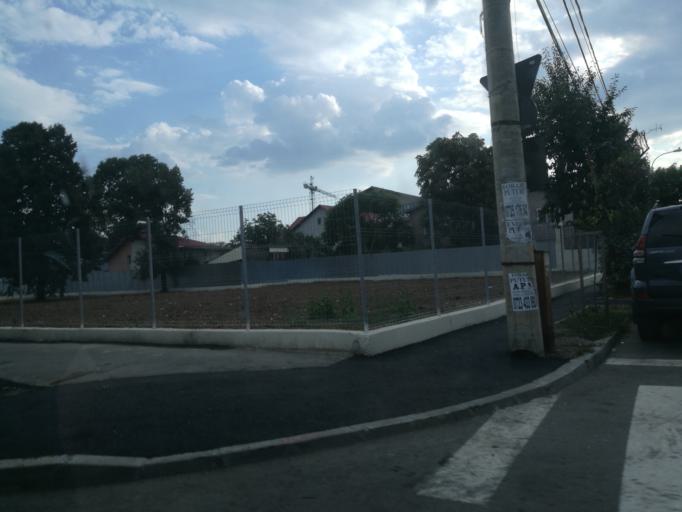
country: RO
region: Ilfov
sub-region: Comuna Chiajna
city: Rosu
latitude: 44.4926
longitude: 26.0331
